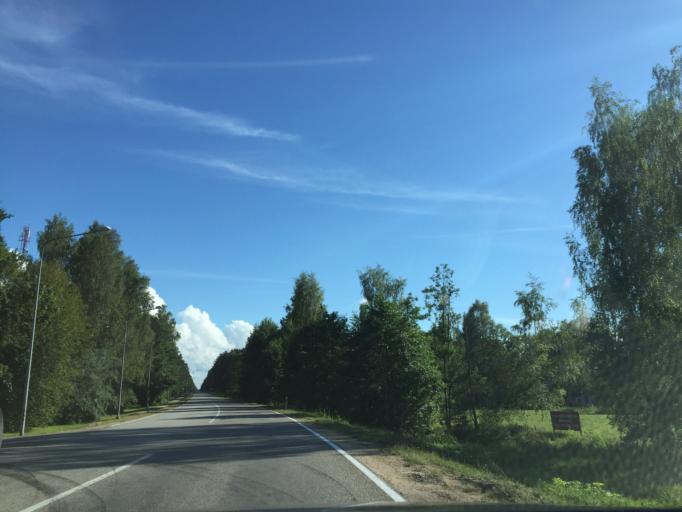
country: LV
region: Riga
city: Jaunciems
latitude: 57.0816
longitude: 24.1597
